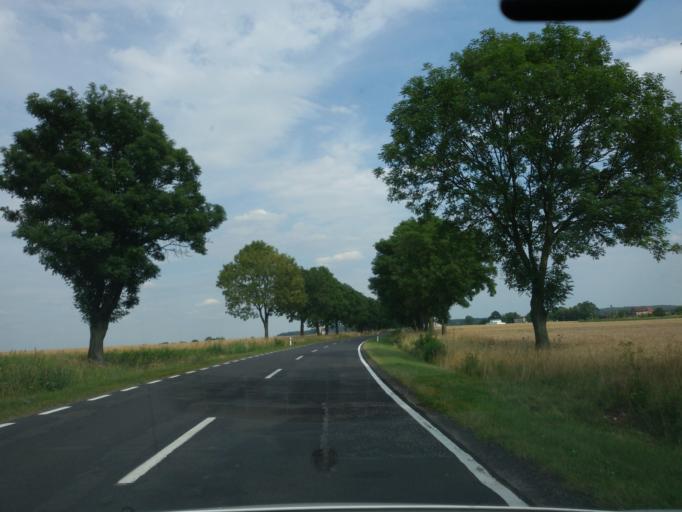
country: PL
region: Lower Silesian Voivodeship
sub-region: Powiat polkowicki
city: Gaworzyce
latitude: 51.6211
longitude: 15.9264
